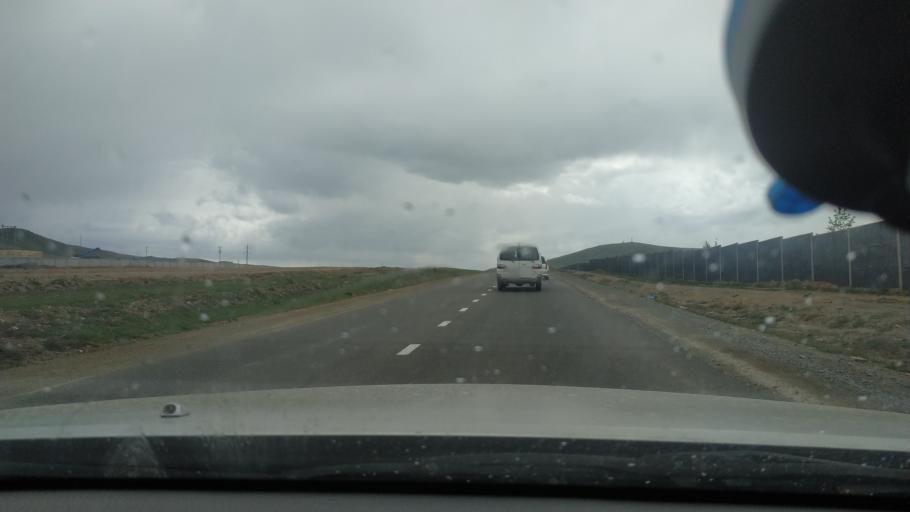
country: MN
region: Ulaanbaatar
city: Ulaanbaatar
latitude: 47.8049
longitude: 106.7491
